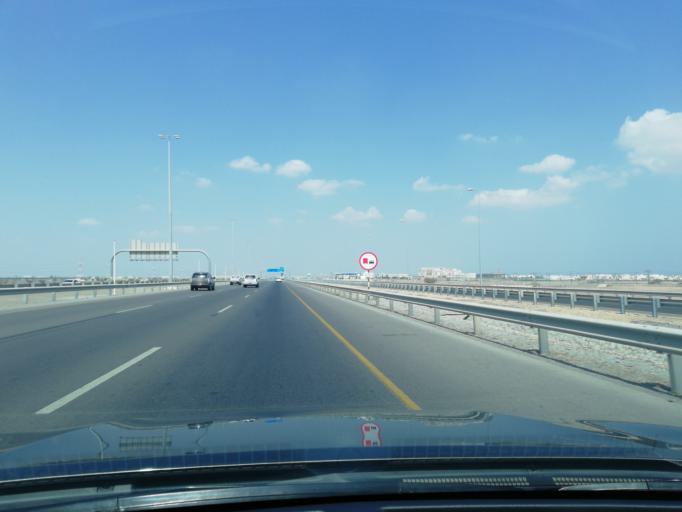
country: OM
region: Muhafazat Masqat
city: As Sib al Jadidah
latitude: 23.6309
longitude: 58.0594
